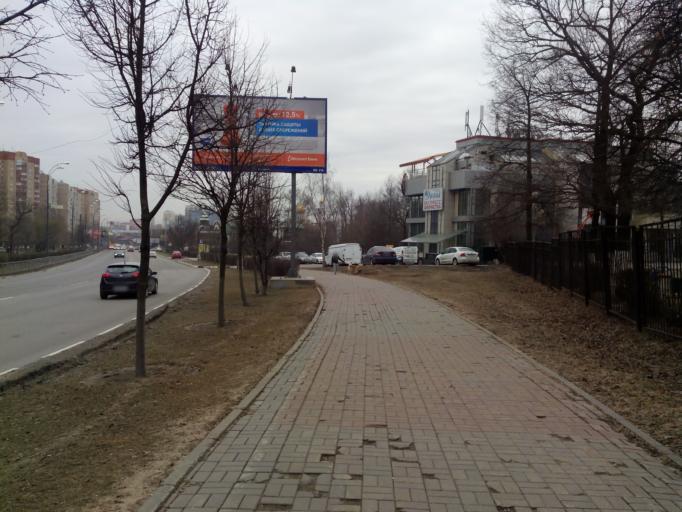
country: RU
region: Moskovskaya
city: Odintsovo
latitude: 55.6820
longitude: 37.2715
